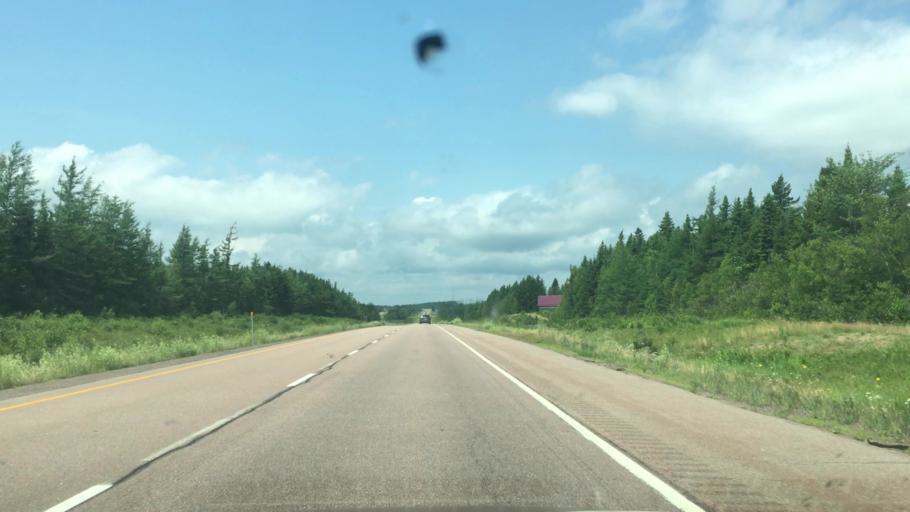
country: CA
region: New Brunswick
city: Sackville
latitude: 45.9828
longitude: -64.4664
